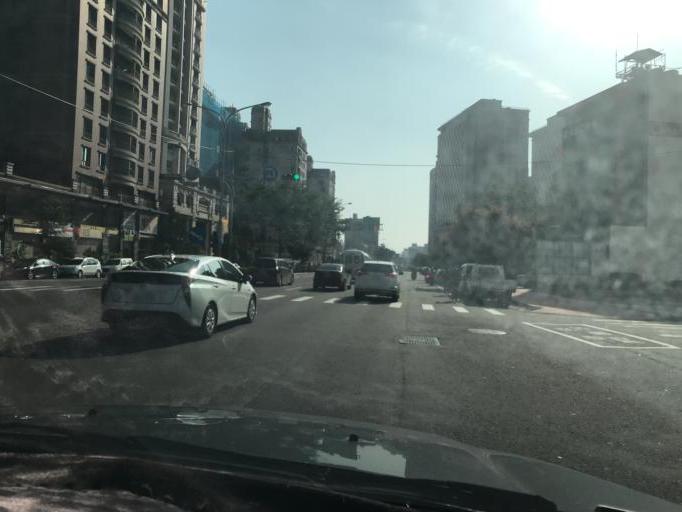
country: TW
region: Taiwan
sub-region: Hsinchu
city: Zhubei
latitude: 24.8229
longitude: 121.0306
